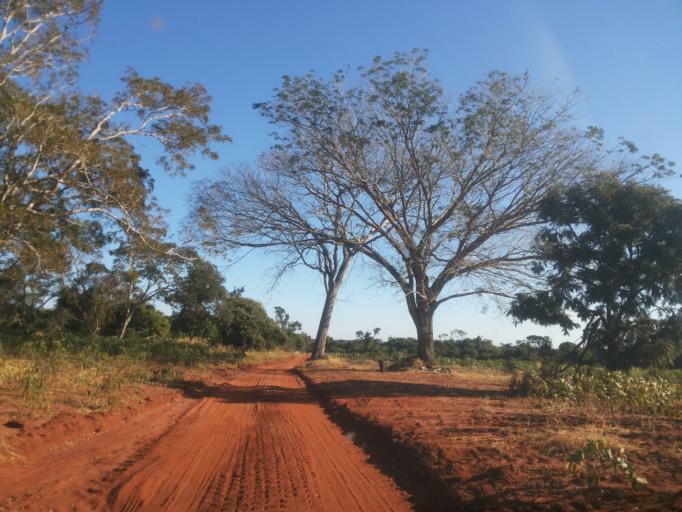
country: BR
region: Minas Gerais
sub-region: Centralina
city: Centralina
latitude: -18.7469
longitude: -49.0932
